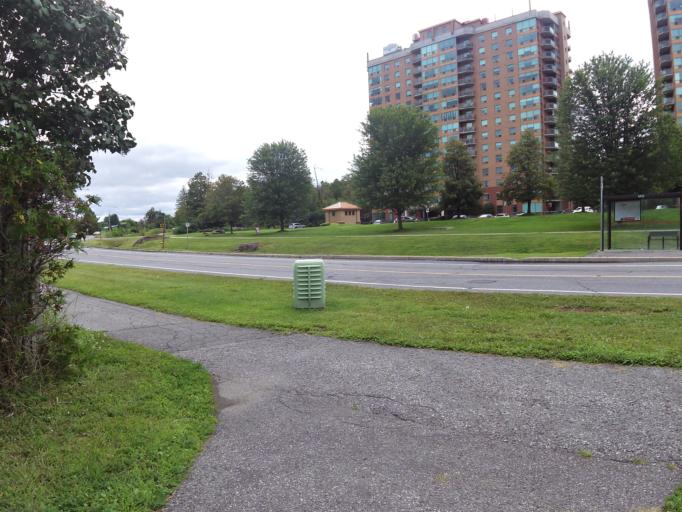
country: CA
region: Ontario
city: Bells Corners
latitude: 45.3142
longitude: -75.9150
